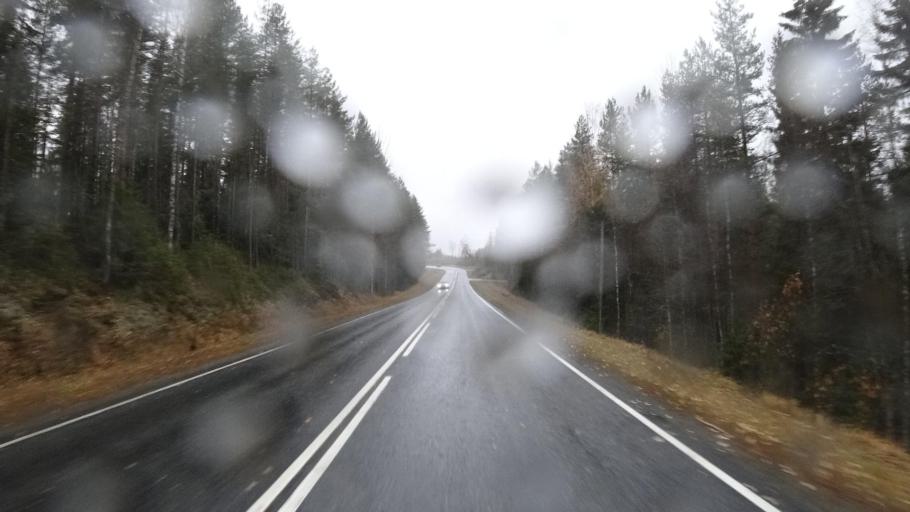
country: FI
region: Northern Savo
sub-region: Koillis-Savo
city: Tuusniemi
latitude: 62.8696
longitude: 28.3909
